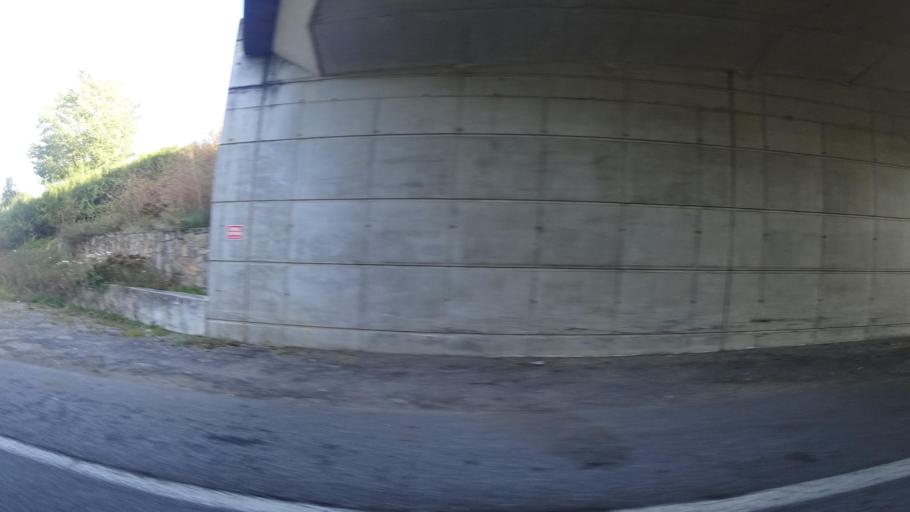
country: FR
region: Midi-Pyrenees
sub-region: Departement de l'Aveyron
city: Olemps
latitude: 44.3277
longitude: 2.5576
